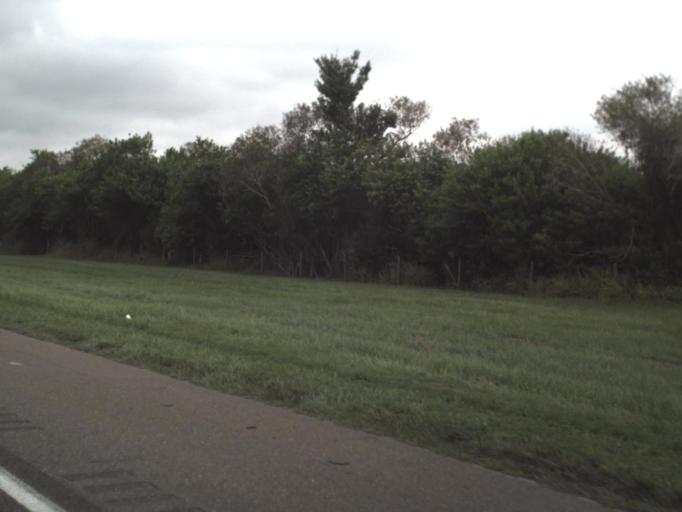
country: US
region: Florida
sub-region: Hillsborough County
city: Ruskin
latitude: 27.6212
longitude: -82.4794
